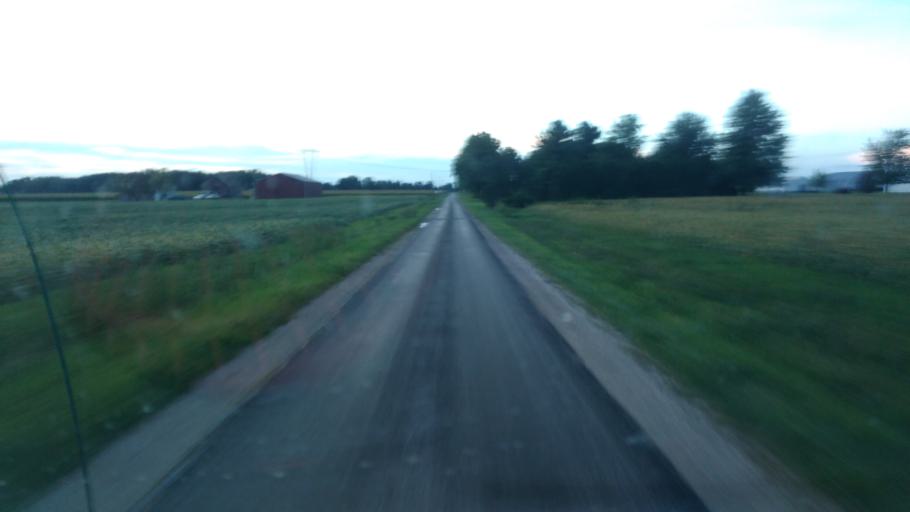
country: US
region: Ohio
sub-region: Crawford County
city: Galion
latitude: 40.7101
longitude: -82.8655
